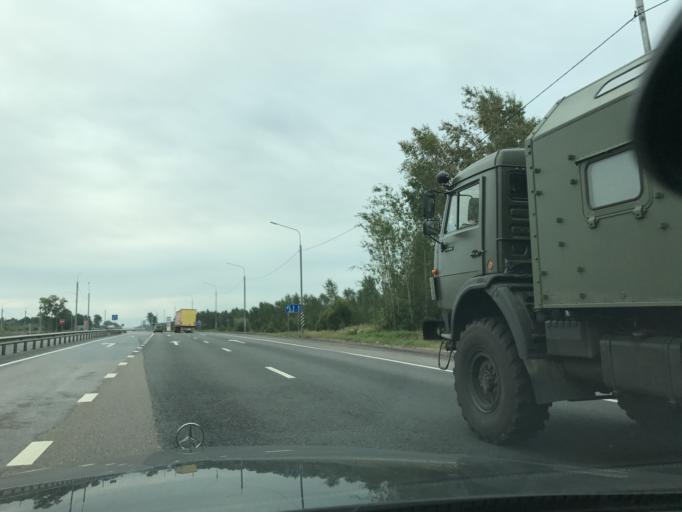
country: RU
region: Vladimir
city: Gorokhovets
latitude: 56.1672
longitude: 42.4628
